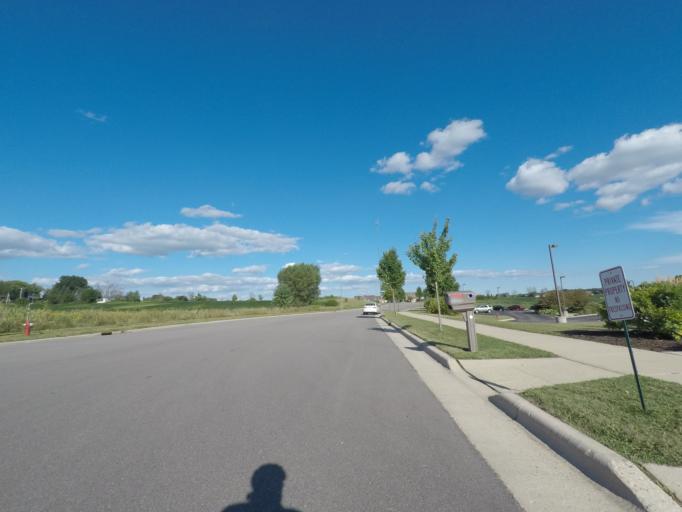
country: US
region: Wisconsin
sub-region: Dane County
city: Middleton
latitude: 43.0581
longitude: -89.5555
